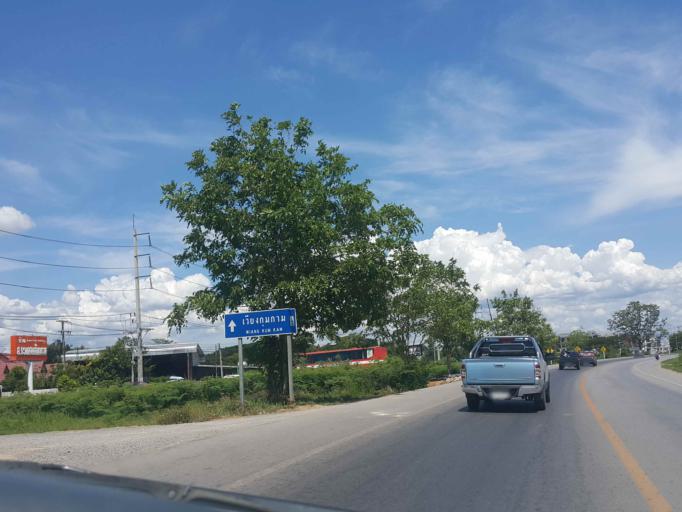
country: TH
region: Chiang Mai
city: San Sai
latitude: 18.8294
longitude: 99.0453
